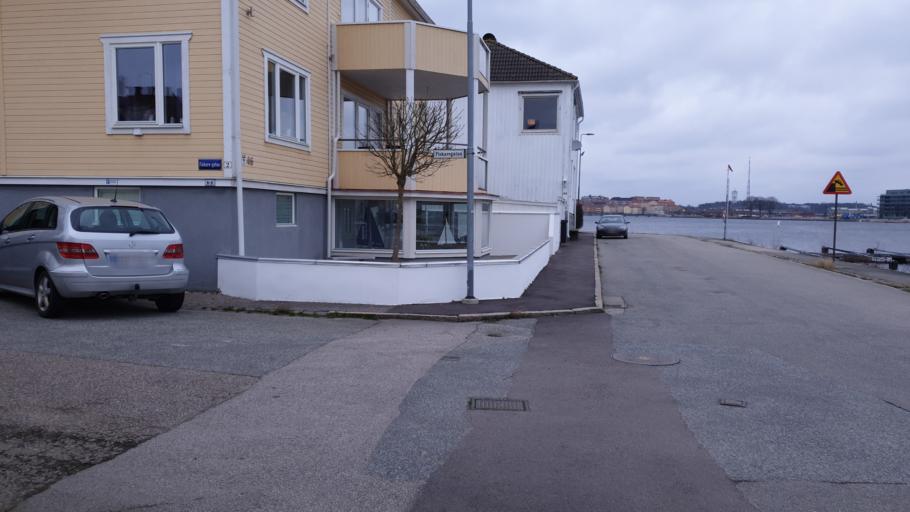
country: SE
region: Blekinge
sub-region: Karlskrona Kommun
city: Karlskrona
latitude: 56.1645
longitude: 15.5733
